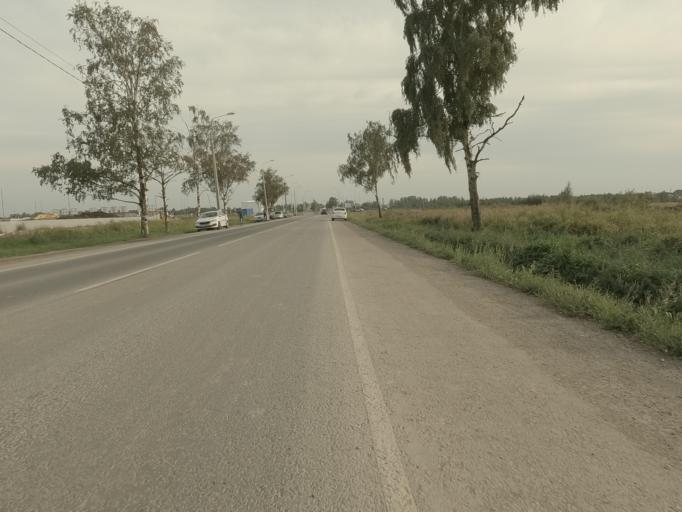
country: RU
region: St.-Petersburg
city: Strel'na
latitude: 59.8431
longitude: 30.0911
